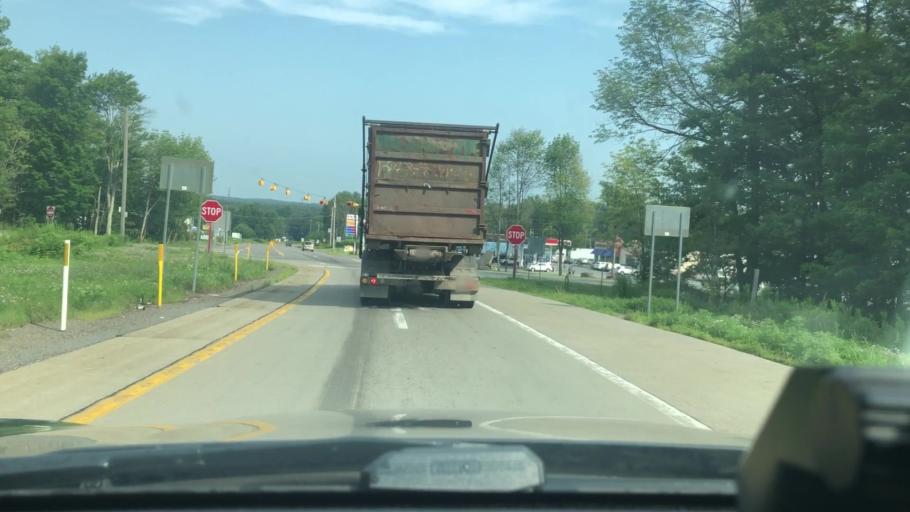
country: US
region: Pennsylvania
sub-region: Lackawanna County
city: Moscow
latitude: 41.2314
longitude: -75.4957
